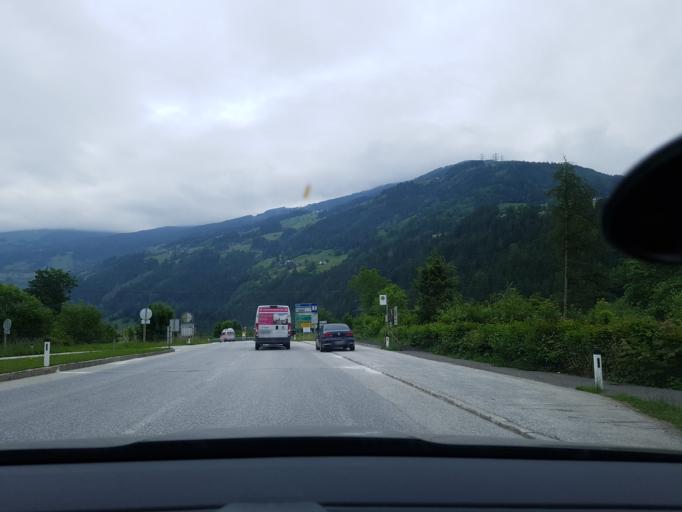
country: AT
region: Tyrol
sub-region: Politischer Bezirk Schwaz
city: Zell am Ziller
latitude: 47.2273
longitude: 11.8879
